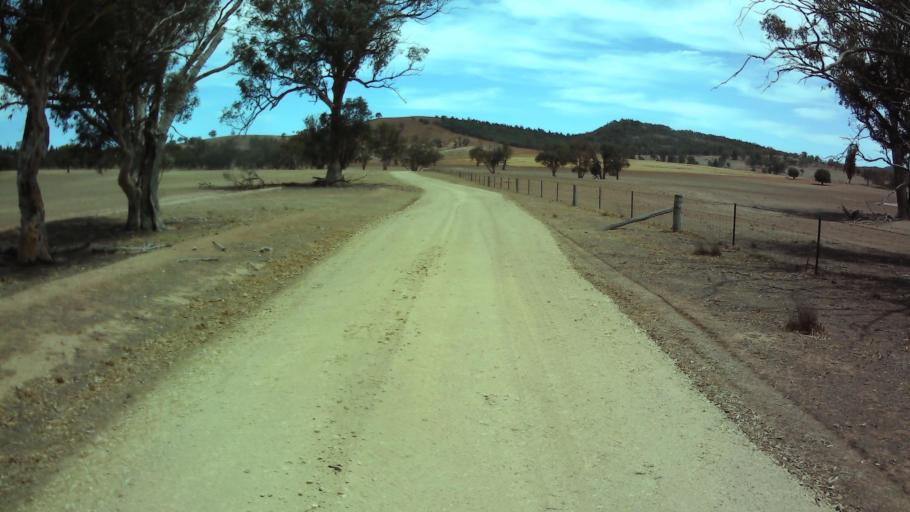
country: AU
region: New South Wales
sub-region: Weddin
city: Grenfell
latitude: -33.7811
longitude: 148.1514
